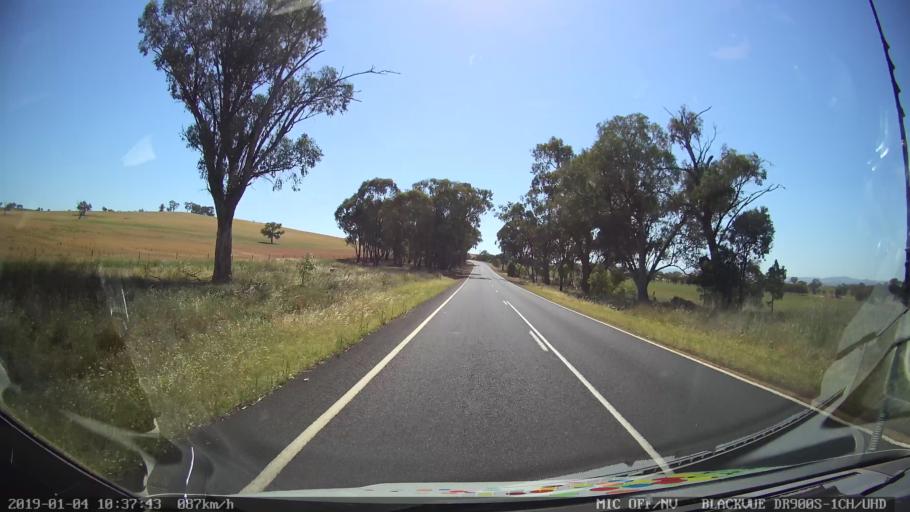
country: AU
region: New South Wales
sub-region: Cabonne
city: Molong
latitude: -33.2952
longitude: 148.6985
